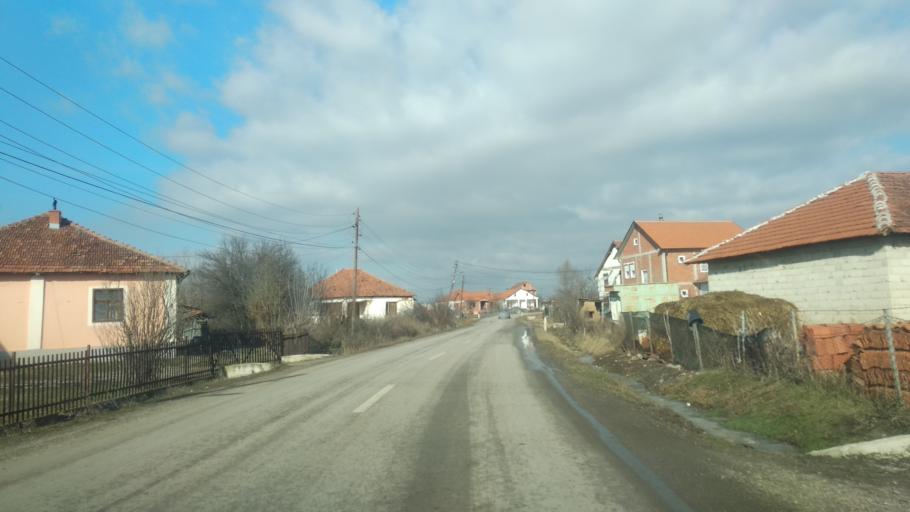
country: XK
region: Pristina
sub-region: Lipjan
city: Lipljan
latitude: 42.5653
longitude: 21.1643
